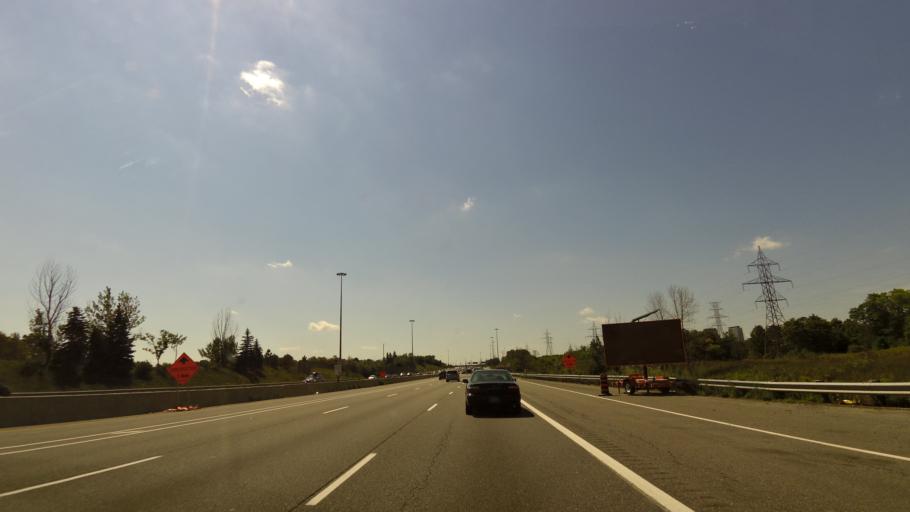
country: CA
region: Ontario
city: Mississauga
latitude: 43.5608
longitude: -79.6862
